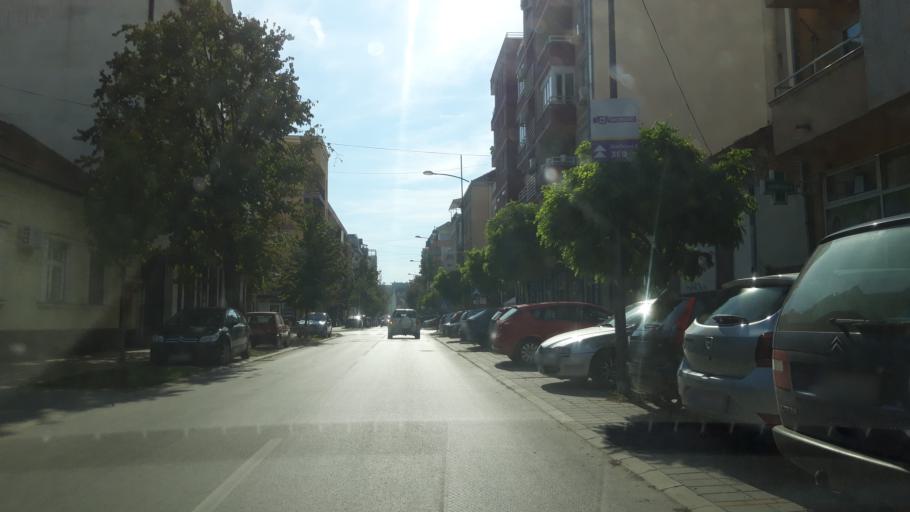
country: RS
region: Autonomna Pokrajina Vojvodina
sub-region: Juznobacki Okrug
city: Novi Sad
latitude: 45.2604
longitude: 19.8498
